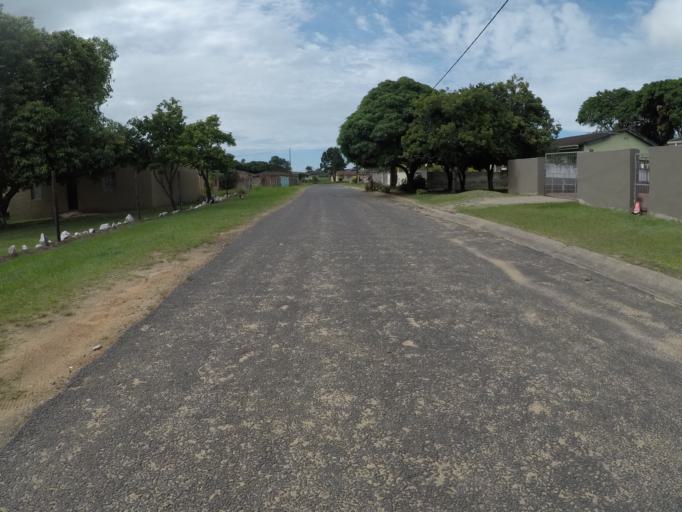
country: ZA
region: KwaZulu-Natal
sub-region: uThungulu District Municipality
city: eSikhawini
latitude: -28.8600
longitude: 31.9212
